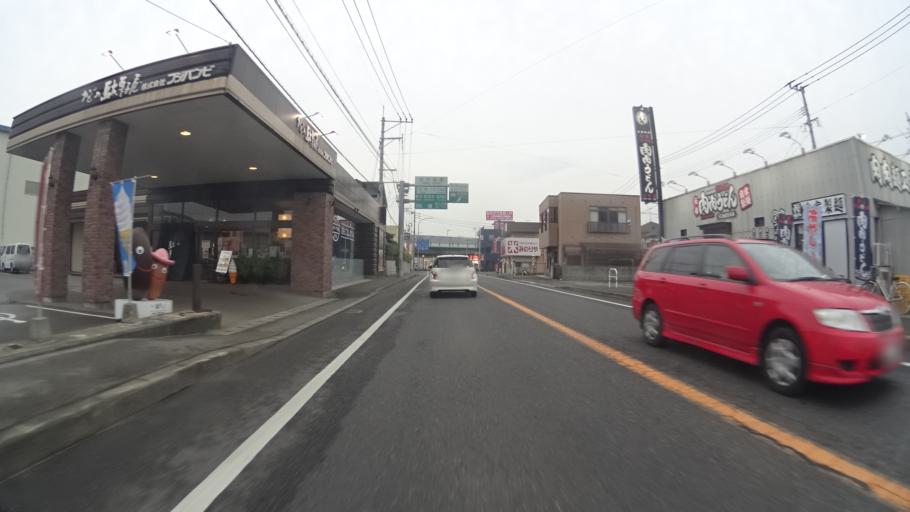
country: JP
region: Fukuoka
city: Onojo
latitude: 33.5235
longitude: 130.4969
